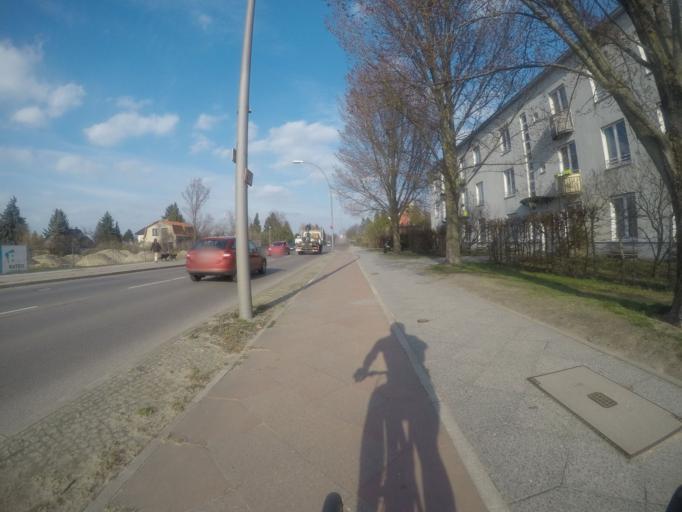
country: DE
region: Berlin
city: Altglienicke
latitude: 52.4161
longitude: 13.5323
